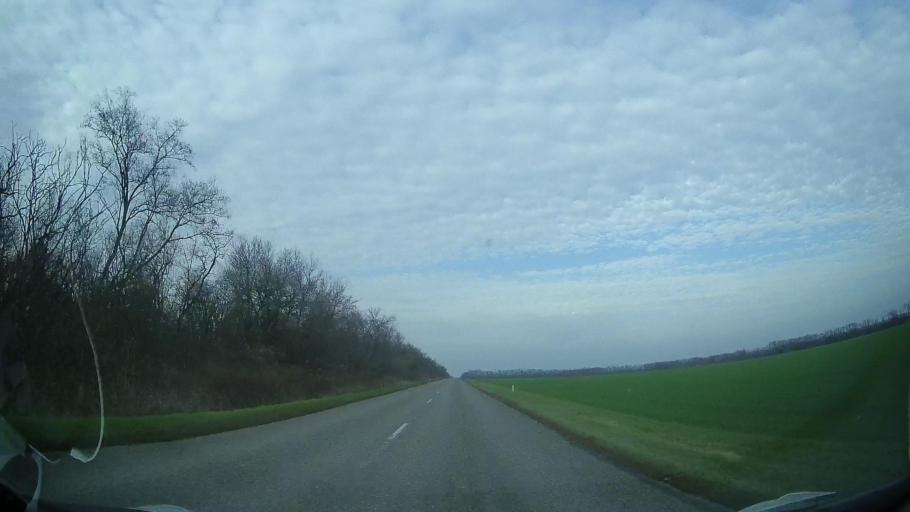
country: RU
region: Rostov
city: Zernograd
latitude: 46.9775
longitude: 40.3916
